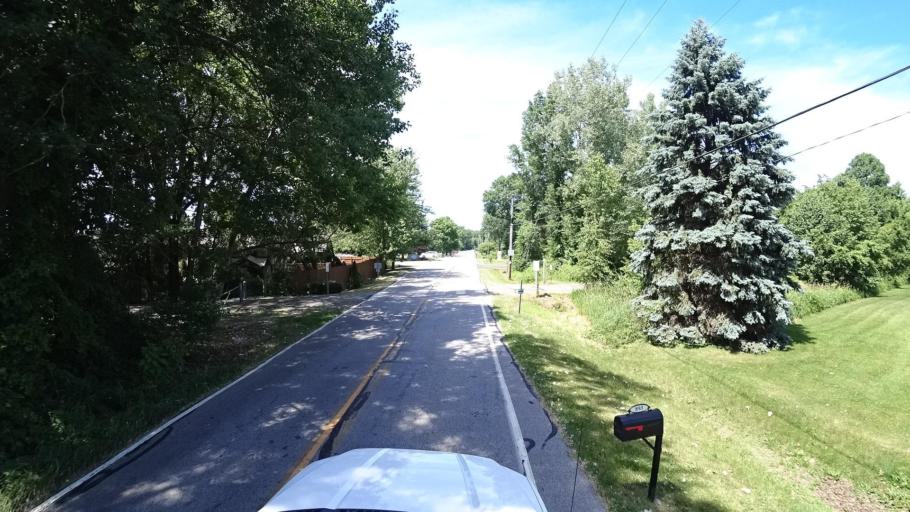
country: US
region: Indiana
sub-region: Porter County
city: Porter
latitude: 41.6027
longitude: -87.0912
